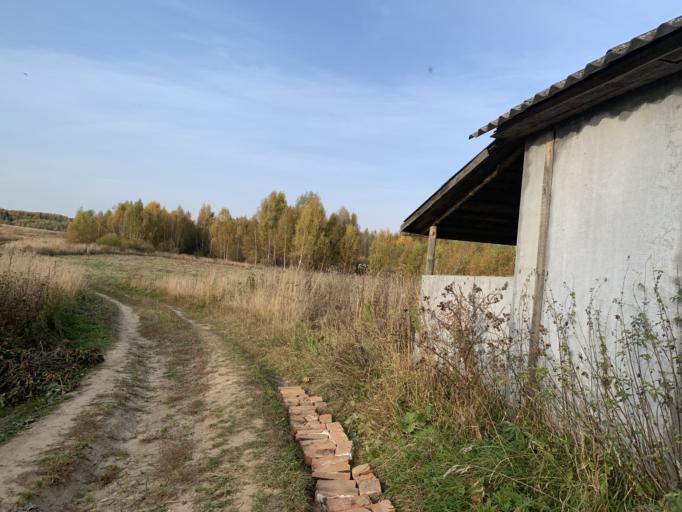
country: RU
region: Jaroslavl
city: Porech'ye-Rybnoye
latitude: 56.9814
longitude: 39.3845
